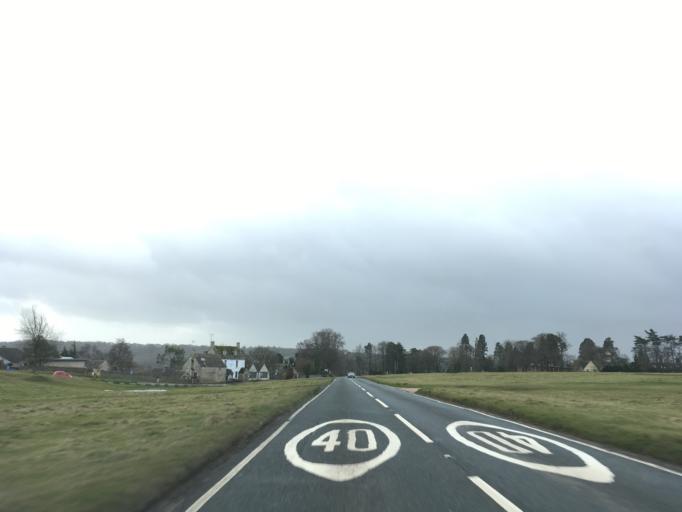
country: GB
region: England
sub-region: Gloucestershire
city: Nailsworth
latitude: 51.7034
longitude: -2.2090
